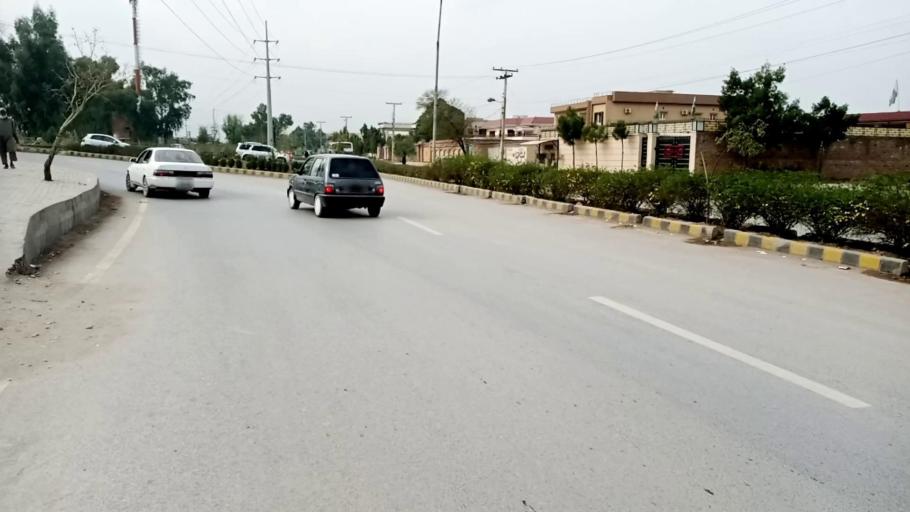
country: PK
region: Khyber Pakhtunkhwa
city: Peshawar
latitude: 33.9599
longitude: 71.4440
